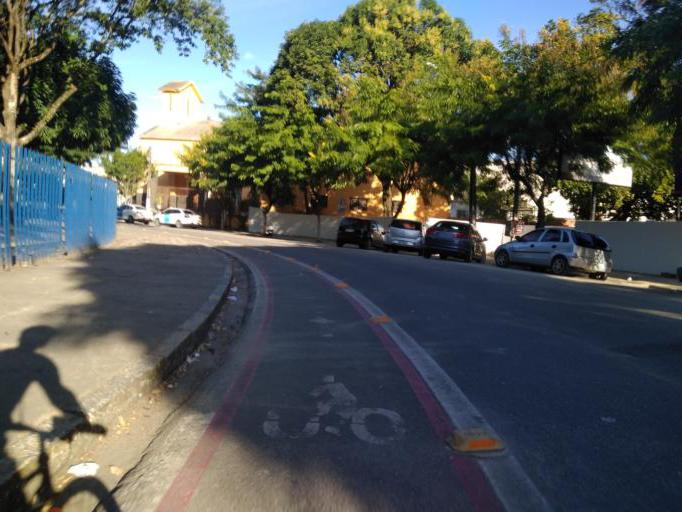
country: BR
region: Pernambuco
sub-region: Recife
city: Recife
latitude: -8.0819
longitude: -34.9387
